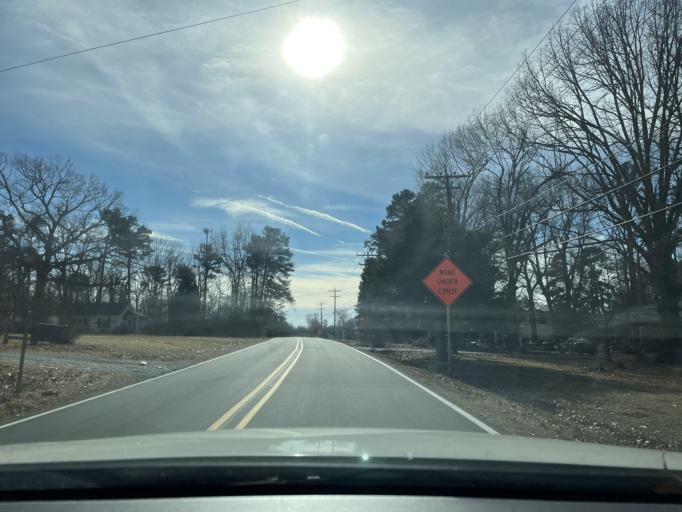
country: US
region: North Carolina
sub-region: Guilford County
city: Pleasant Garden
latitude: 36.0156
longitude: -79.7781
